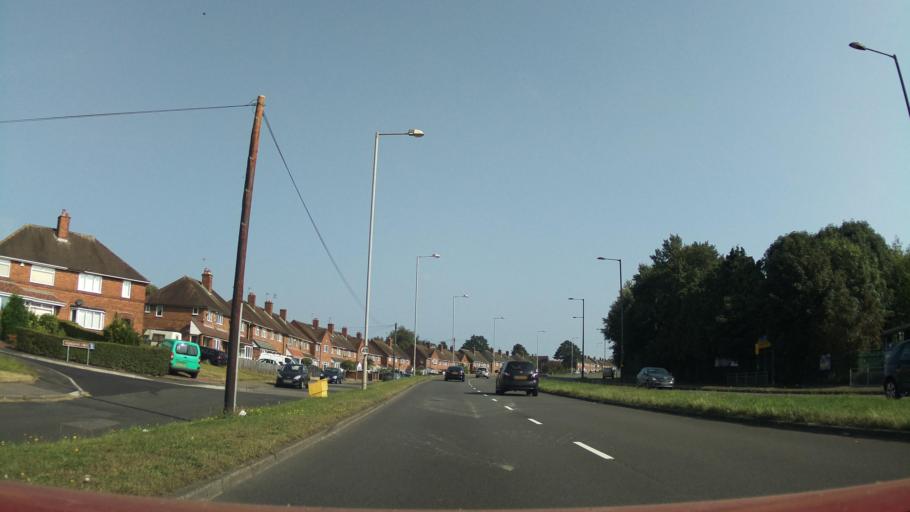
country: GB
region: England
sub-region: Walsall
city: Streetly
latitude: 52.5575
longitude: -1.8977
